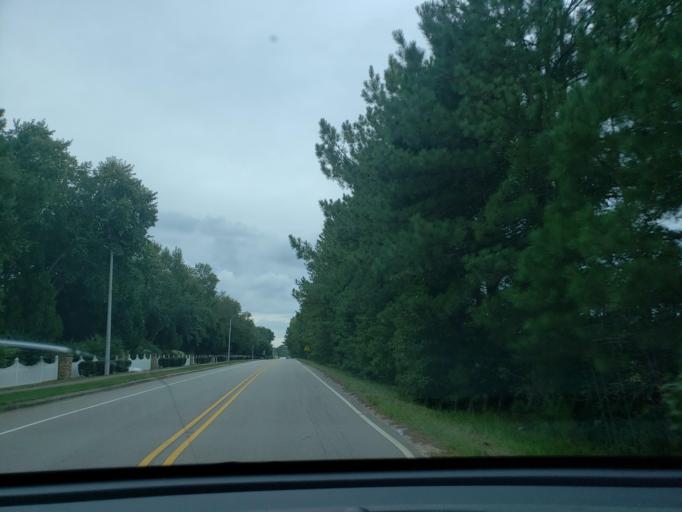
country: US
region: North Carolina
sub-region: Wake County
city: Green Level
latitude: 35.8105
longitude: -78.8709
